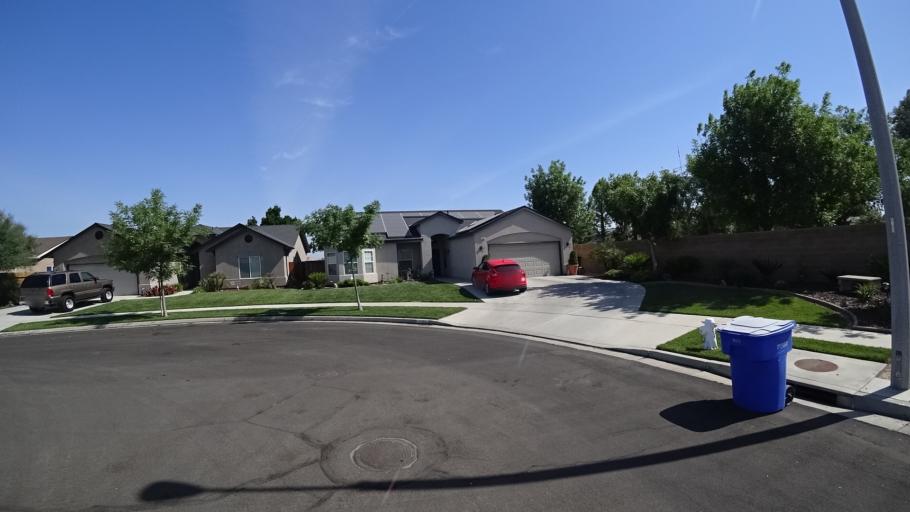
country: US
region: California
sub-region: Kings County
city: Hanford
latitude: 36.3446
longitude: -119.6665
